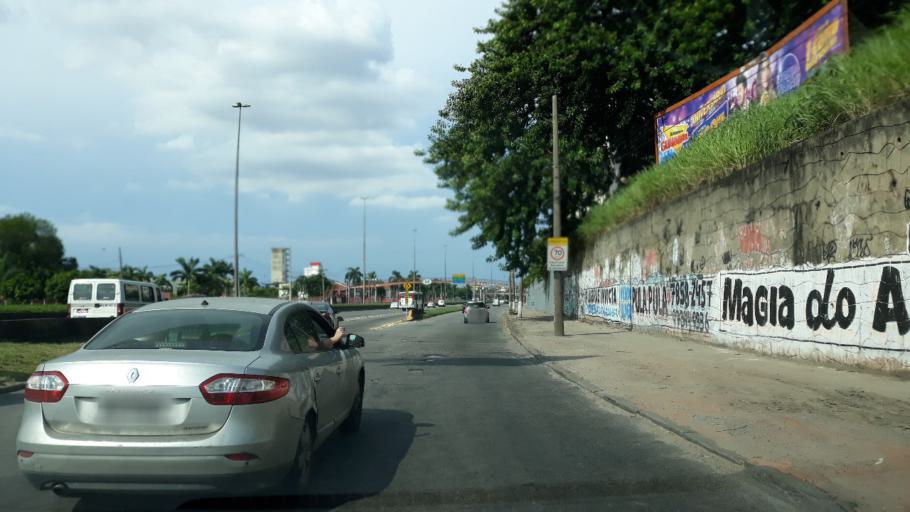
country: BR
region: Rio de Janeiro
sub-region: Sao Joao De Meriti
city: Sao Joao de Meriti
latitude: -22.8496
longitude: -43.3837
